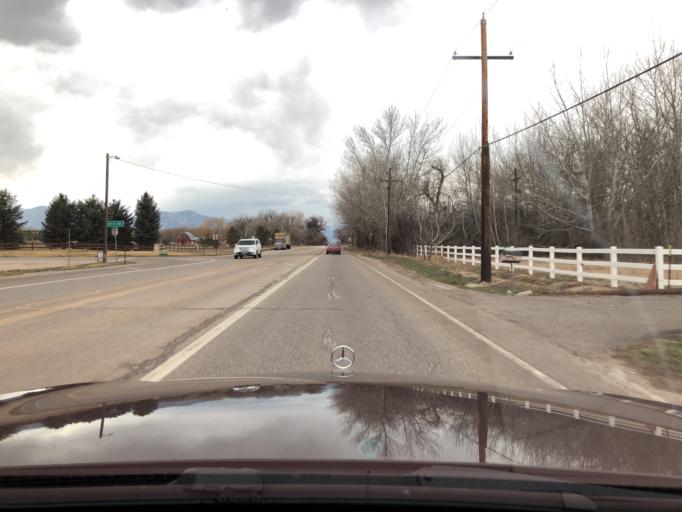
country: US
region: Colorado
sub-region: Boulder County
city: Louisville
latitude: 40.0147
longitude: -105.1398
